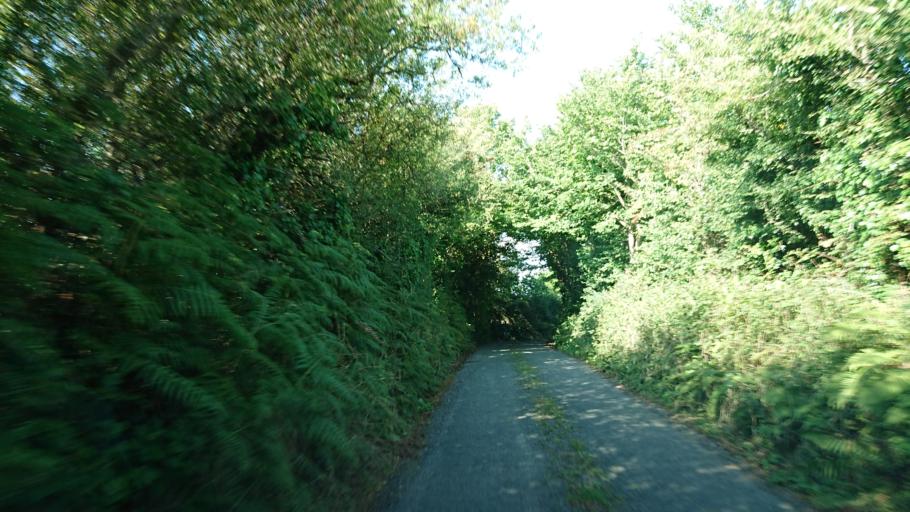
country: IE
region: Munster
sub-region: Waterford
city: Waterford
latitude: 52.2055
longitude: -7.0579
